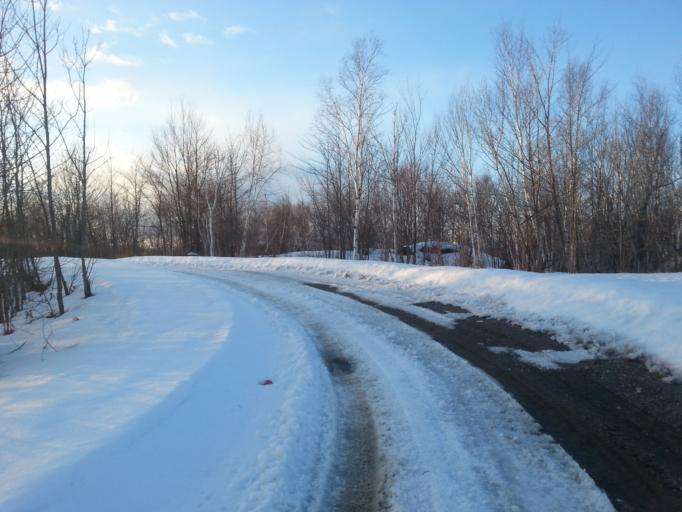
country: CA
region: Ontario
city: Greater Sudbury
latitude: 46.5903
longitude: -80.9860
